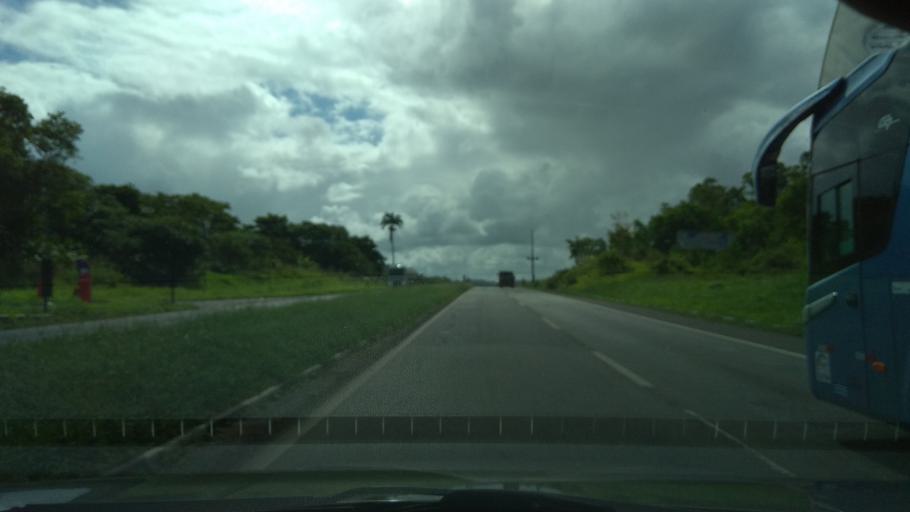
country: BR
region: Bahia
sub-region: Simoes Filho
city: Simoes Filho
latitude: -12.7725
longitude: -38.4195
